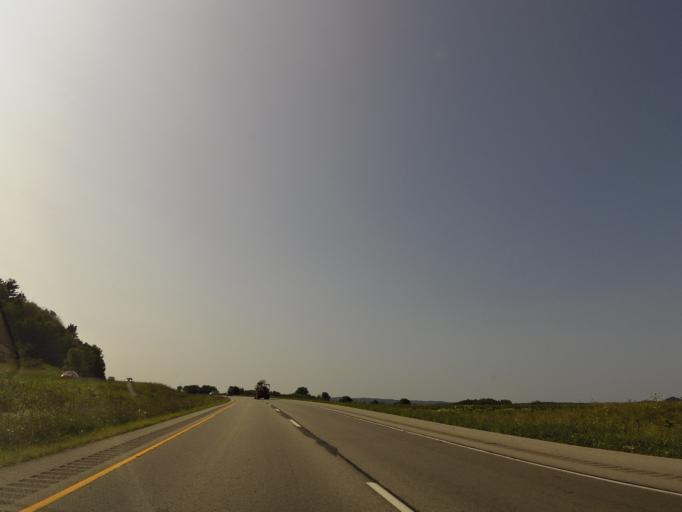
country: US
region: Wisconsin
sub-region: La Crosse County
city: Bangor
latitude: 43.8898
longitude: -91.0194
